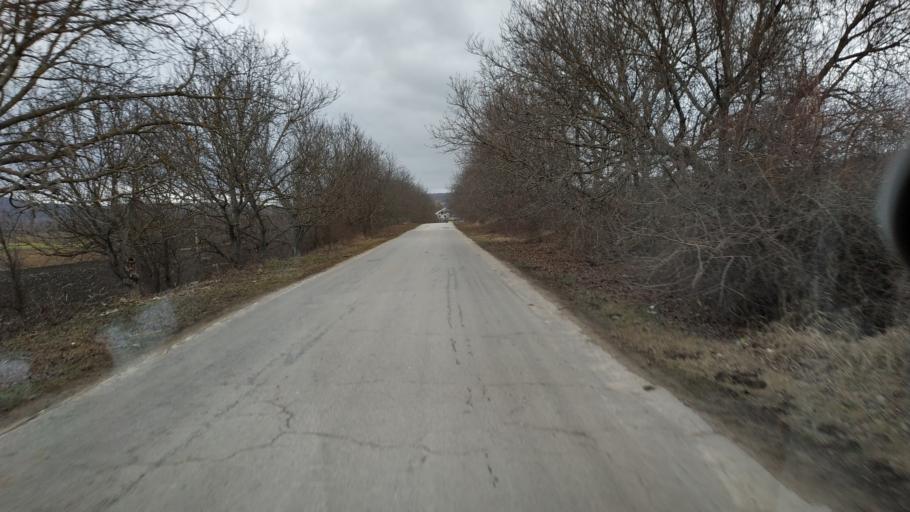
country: MD
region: Calarasi
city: Calarasi
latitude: 47.2491
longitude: 28.1526
